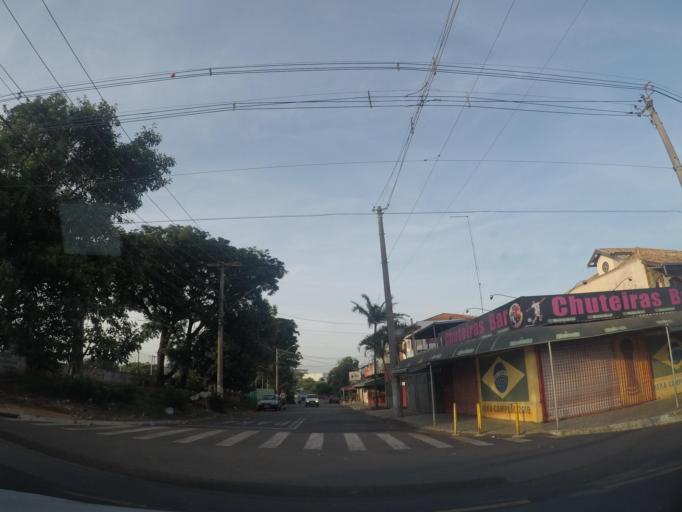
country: BR
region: Sao Paulo
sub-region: Hortolandia
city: Hortolandia
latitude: -22.8467
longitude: -47.1691
